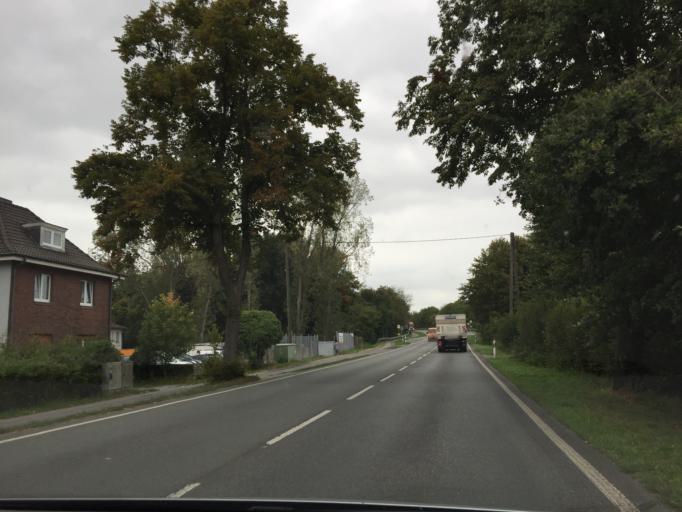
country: DE
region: North Rhine-Westphalia
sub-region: Regierungsbezirk Dusseldorf
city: Wesel
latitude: 51.6380
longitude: 6.6422
